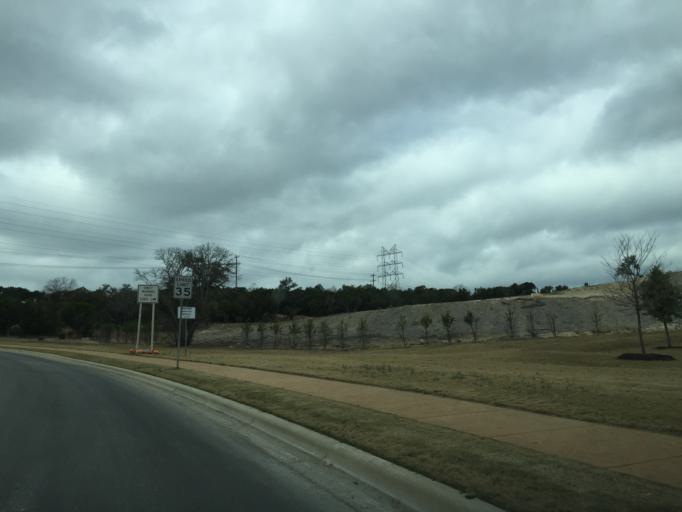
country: US
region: Texas
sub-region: Travis County
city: The Hills
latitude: 30.3499
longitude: -98.0156
